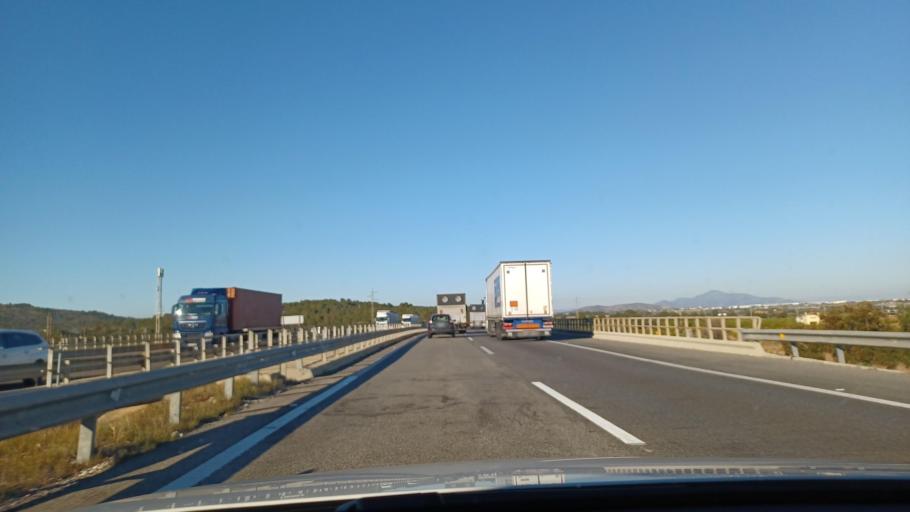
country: ES
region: Valencia
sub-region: Provincia de Castello
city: Calig
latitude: 40.4081
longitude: 0.3706
